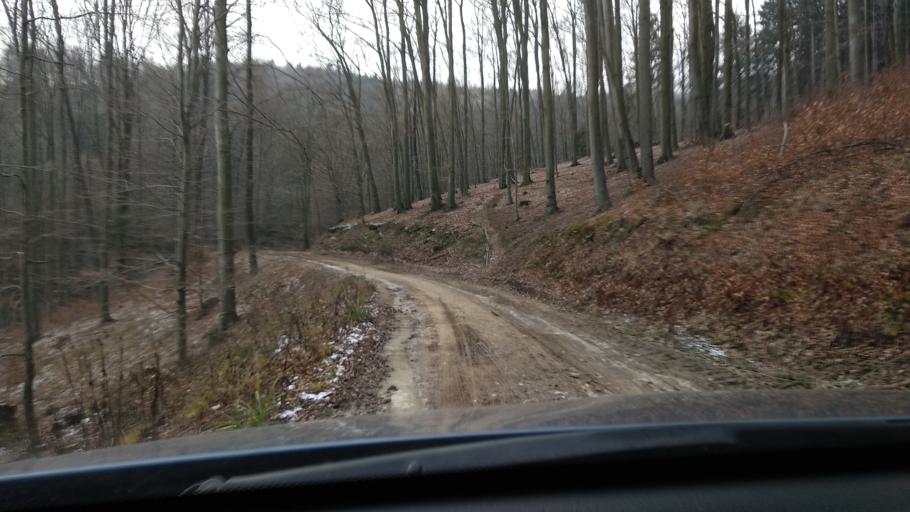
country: SK
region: Trenciansky
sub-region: Okres Trencin
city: Trencin
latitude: 48.7991
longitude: 18.0704
